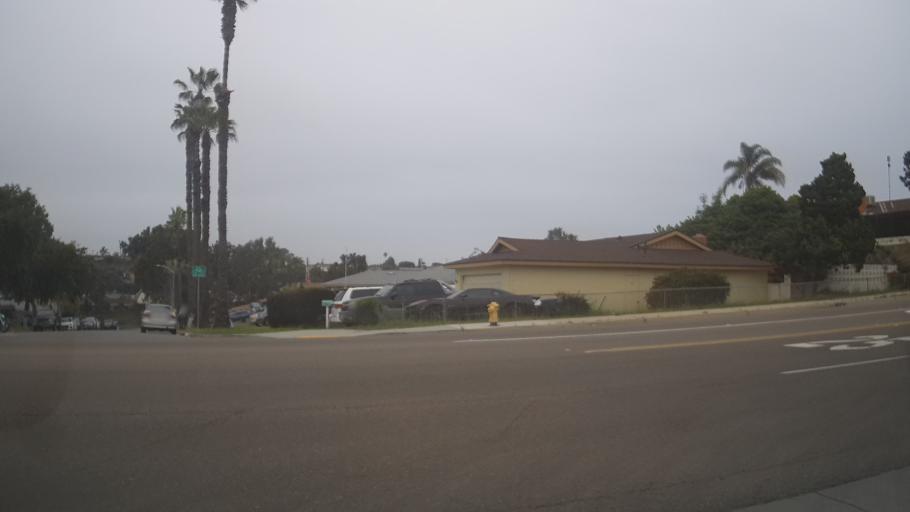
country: US
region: California
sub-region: San Diego County
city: Bonita
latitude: 32.6268
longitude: -117.0493
